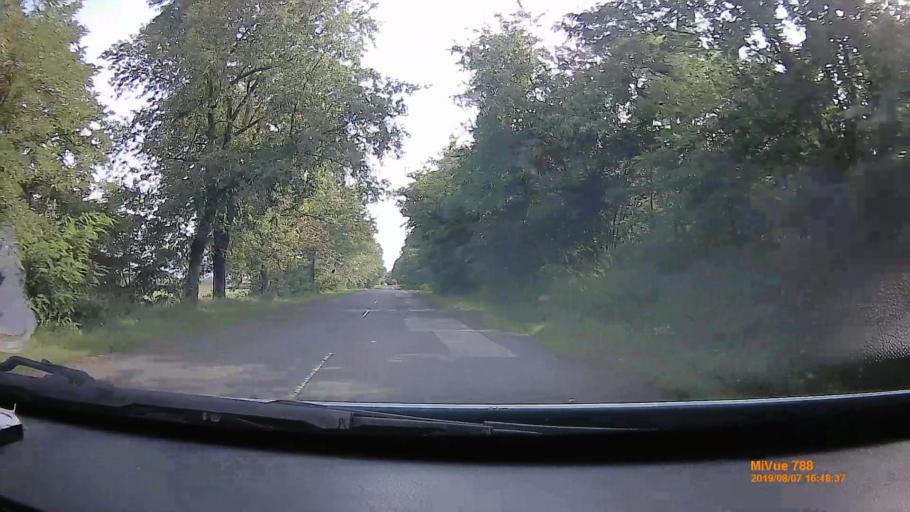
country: HU
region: Borsod-Abauj-Zemplen
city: Abaujszanto
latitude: 48.3295
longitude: 21.2031
